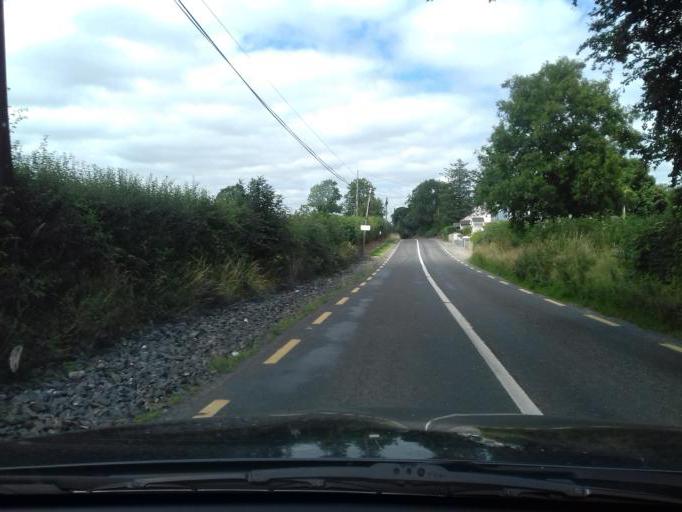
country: IE
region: Leinster
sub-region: County Carlow
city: Tullow
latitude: 52.8143
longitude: -6.7259
